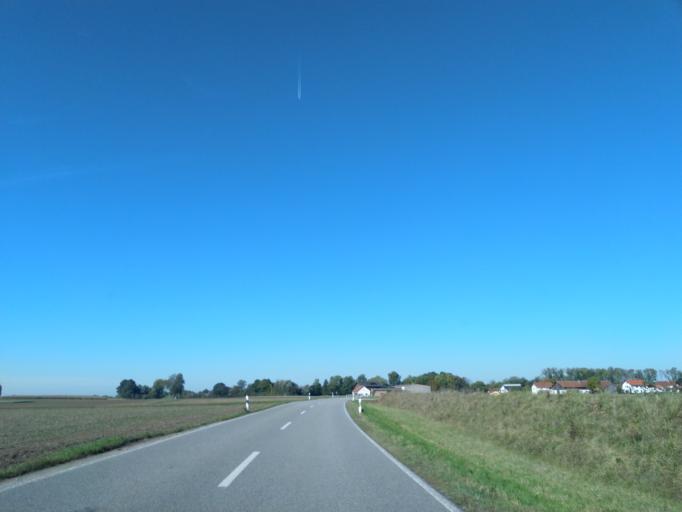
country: DE
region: Bavaria
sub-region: Lower Bavaria
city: Offenberg
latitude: 48.8226
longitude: 12.8699
